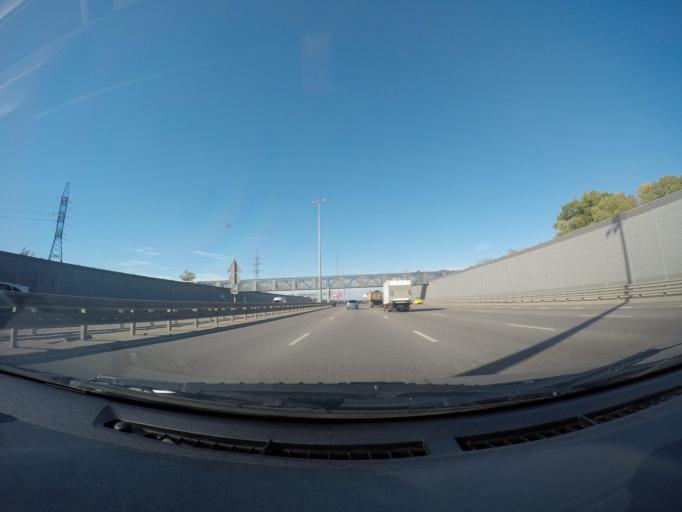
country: RU
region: Moskovskaya
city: Tomilino
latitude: 55.6323
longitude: 37.9356
